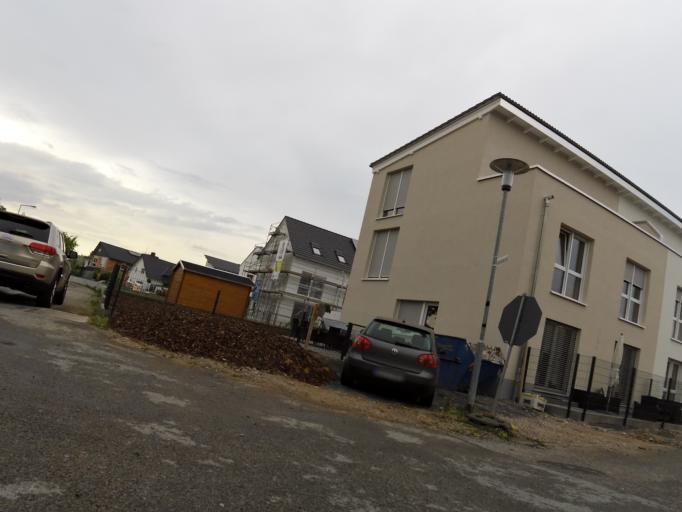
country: DE
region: Hesse
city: Dieburg
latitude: 49.8980
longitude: 8.8546
